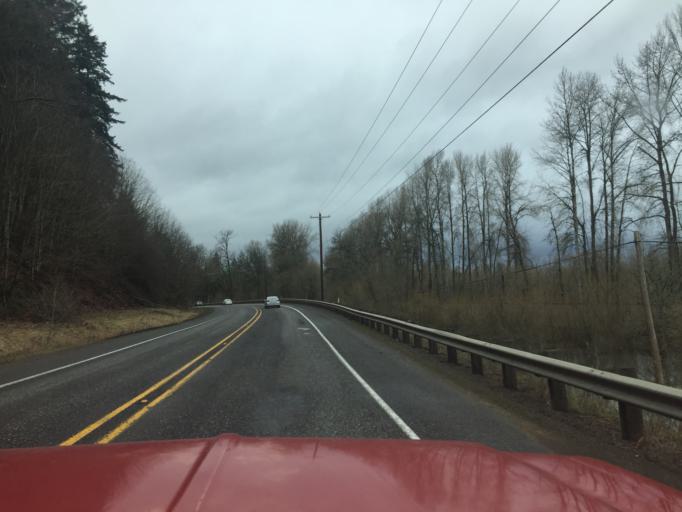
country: US
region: Washington
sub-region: Cowlitz County
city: Kalama
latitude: 46.0254
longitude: -122.8829
